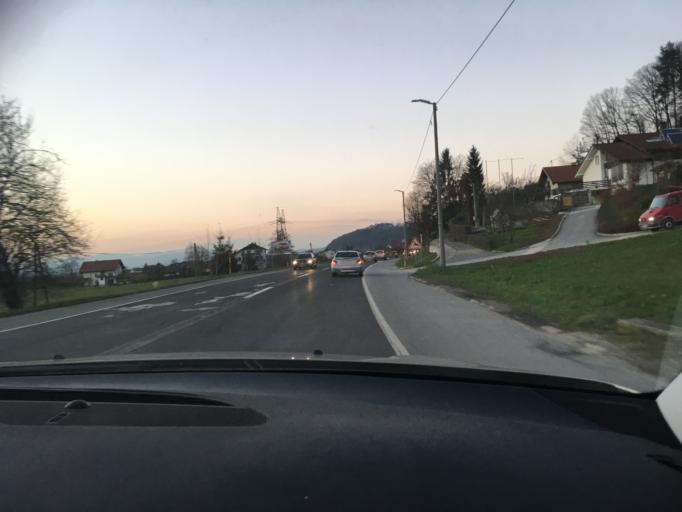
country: SI
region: Skofljica
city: Lavrica
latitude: 45.9920
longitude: 14.5634
